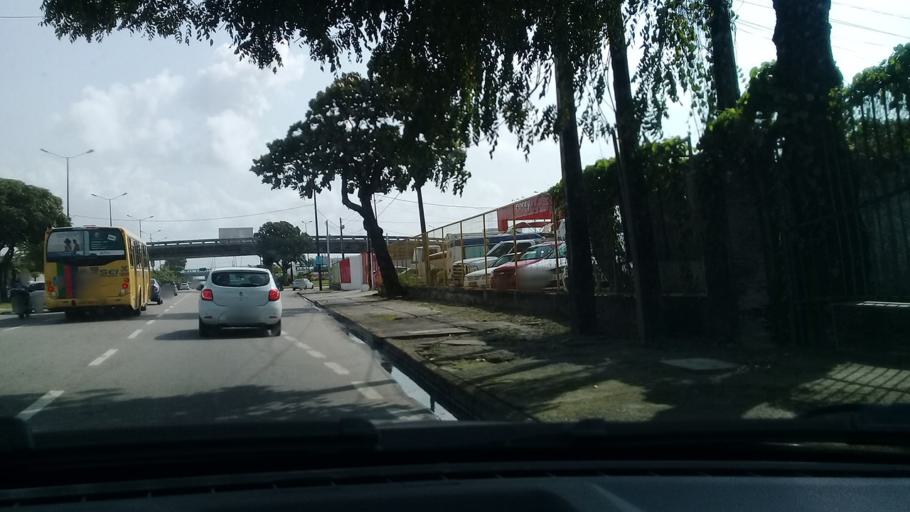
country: BR
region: Pernambuco
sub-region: Recife
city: Recife
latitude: -8.1379
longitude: -34.9171
